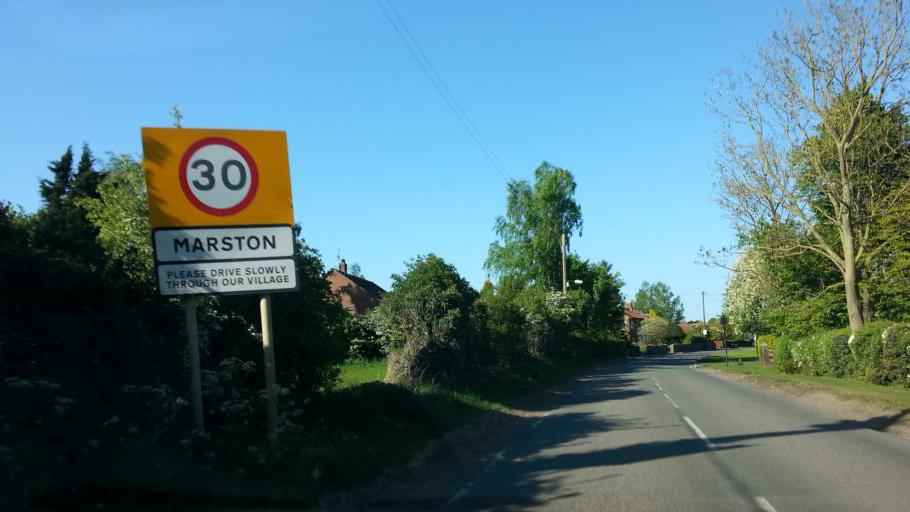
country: GB
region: England
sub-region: Lincolnshire
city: Great Gonerby
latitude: 52.9795
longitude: -0.6770
